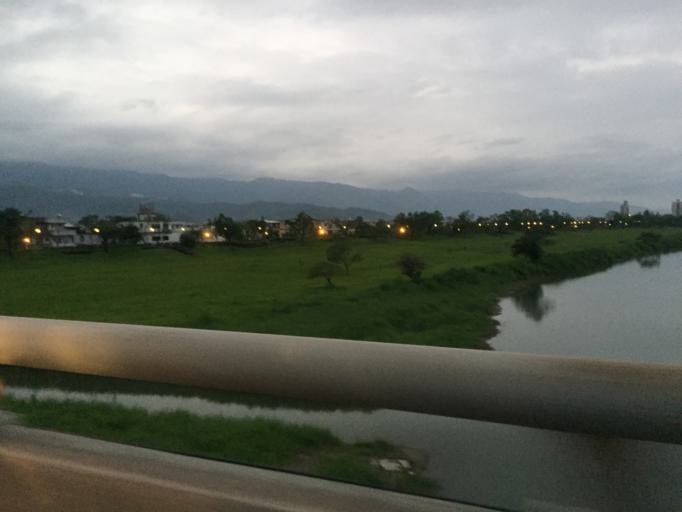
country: TW
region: Taiwan
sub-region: Yilan
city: Yilan
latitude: 24.7581
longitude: 121.7439
